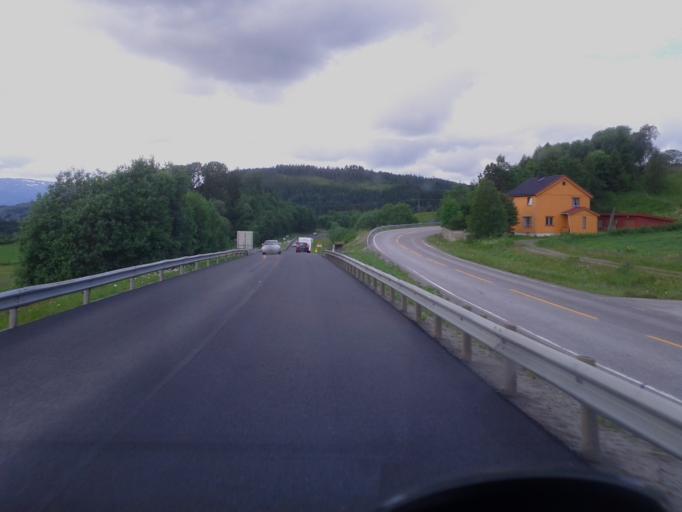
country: NO
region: Nord-Trondelag
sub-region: Grong
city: Grong
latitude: 64.5307
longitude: 12.4030
